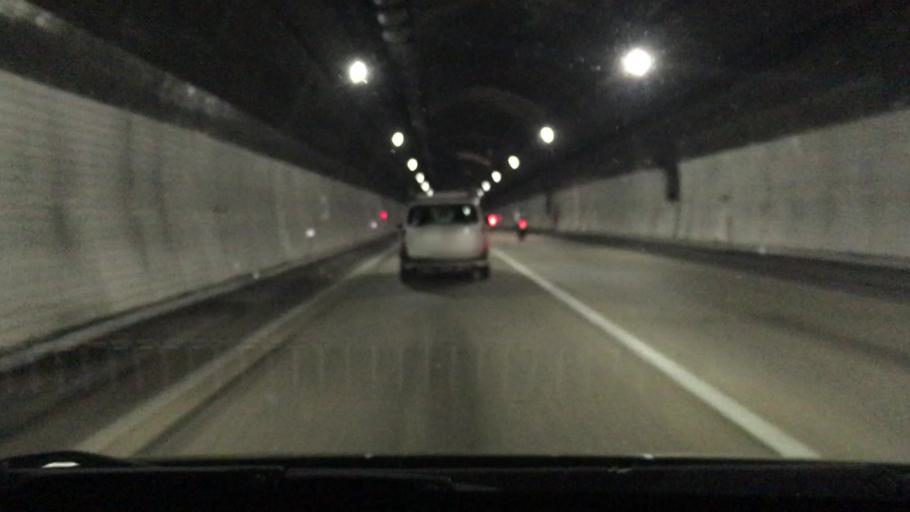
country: JP
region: Hiroshima
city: Hatsukaichi
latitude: 34.3828
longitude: 132.3927
